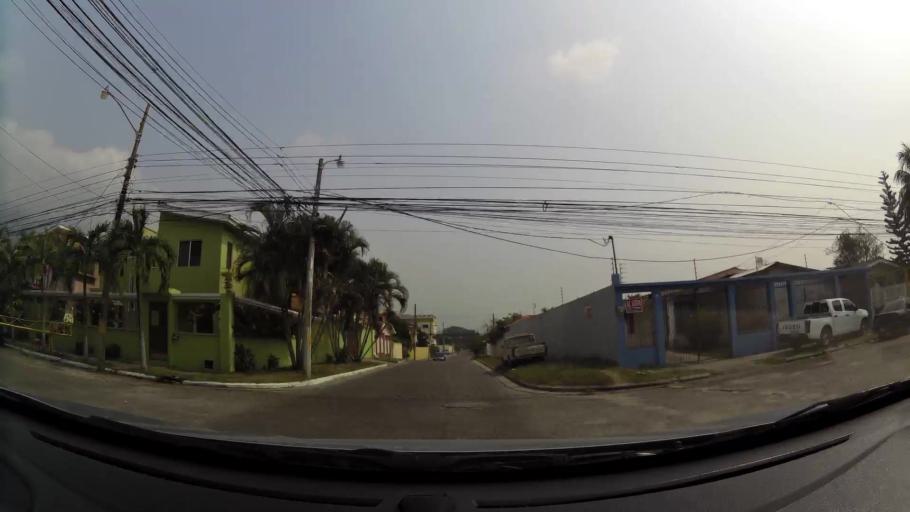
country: HN
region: Cortes
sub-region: San Pedro Sula
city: Pena Blanca
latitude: 15.5338
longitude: -88.0310
